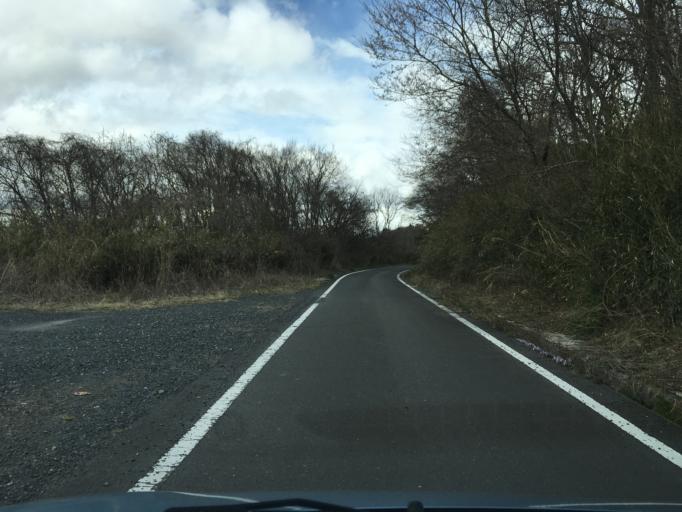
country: JP
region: Miyagi
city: Wakuya
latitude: 38.6829
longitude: 141.1079
